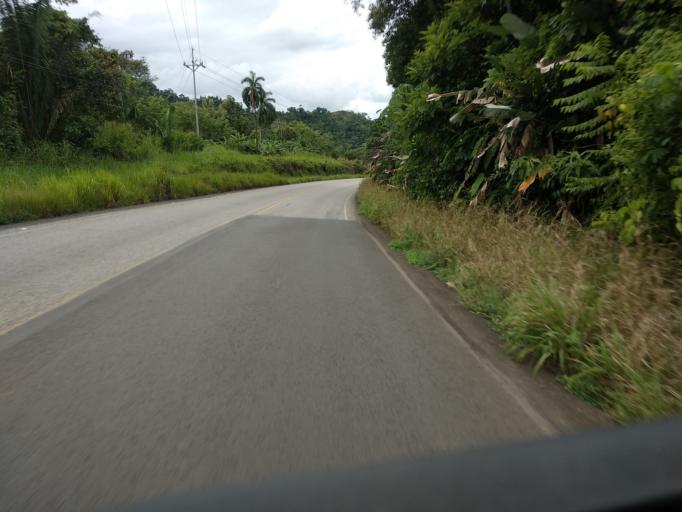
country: CR
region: Puntarenas
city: Buenos Aires
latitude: 9.1126
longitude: -83.2902
